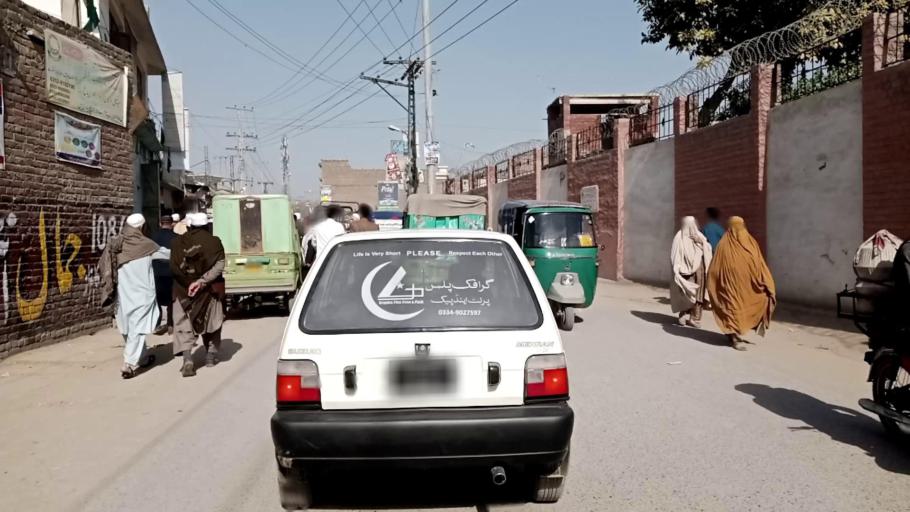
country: PK
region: Khyber Pakhtunkhwa
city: Peshawar
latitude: 33.9937
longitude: 71.5794
